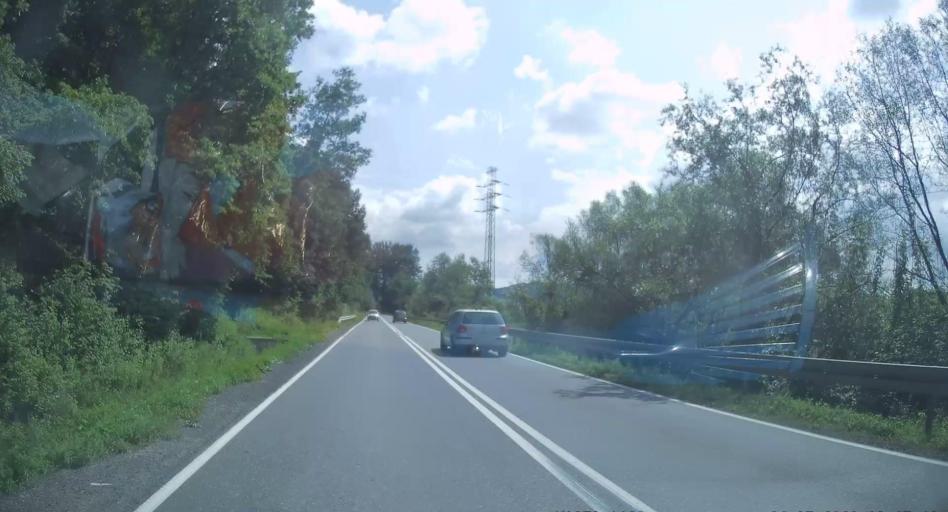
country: PL
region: Lesser Poland Voivodeship
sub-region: Powiat tarnowski
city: Zakliczyn
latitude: 49.8759
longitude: 20.8248
